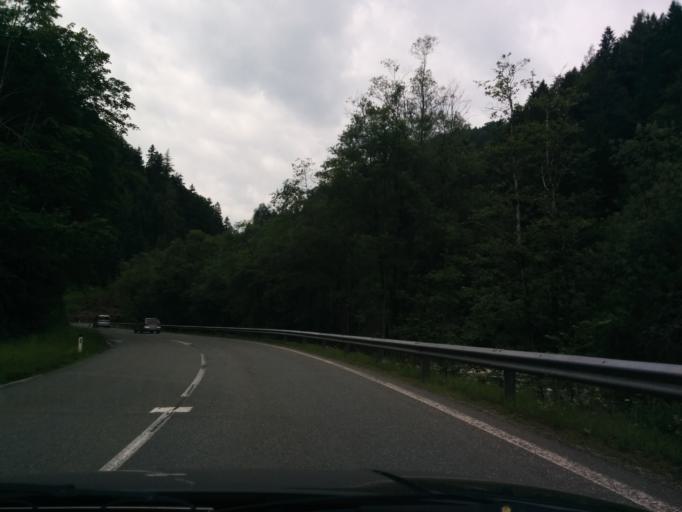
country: AT
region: Salzburg
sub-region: Politischer Bezirk Hallein
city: Abtenau
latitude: 47.5952
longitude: 13.2987
